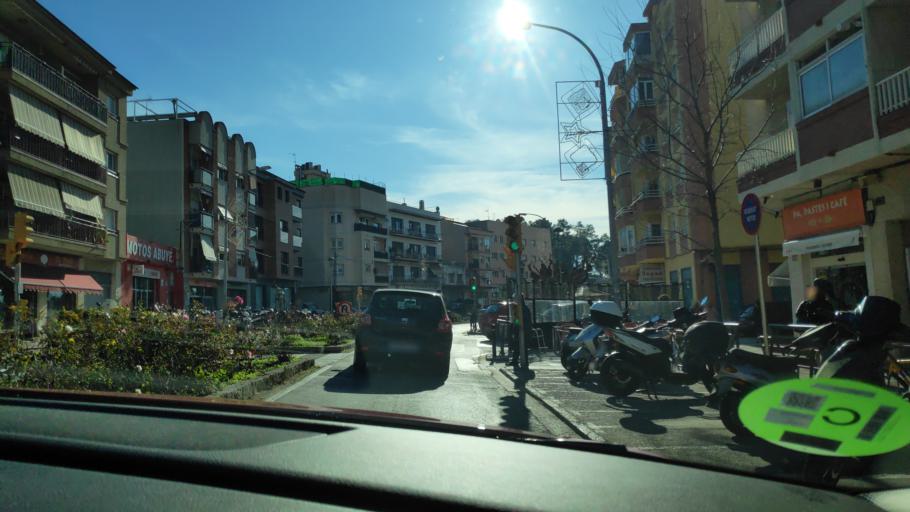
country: ES
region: Catalonia
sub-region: Provincia de Girona
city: Lloret de Mar
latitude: 41.7083
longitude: 2.8416
